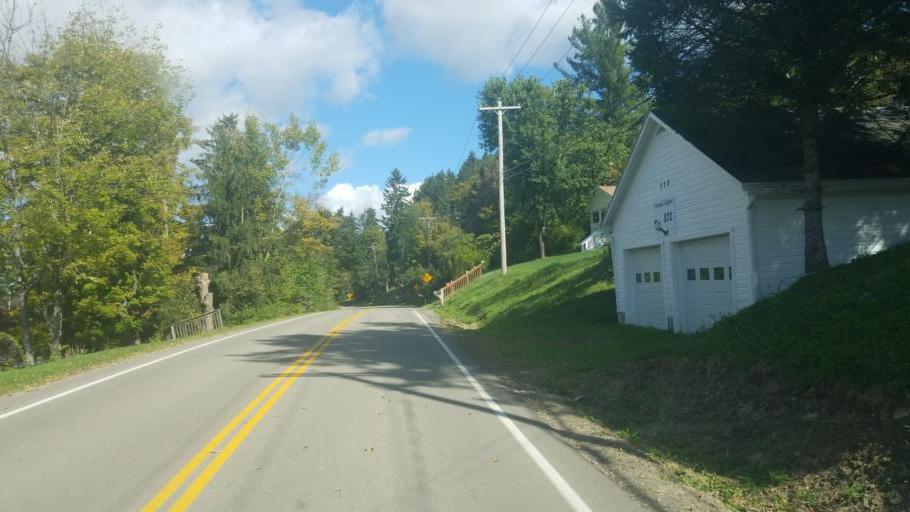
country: US
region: New York
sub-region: Allegany County
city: Cuba
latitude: 42.2571
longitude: -78.2923
